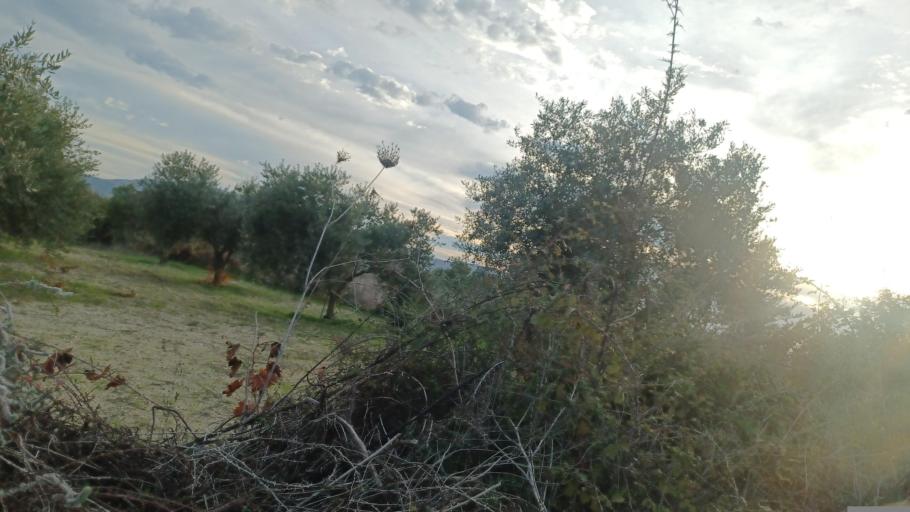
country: CY
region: Pafos
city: Mesogi
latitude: 34.8659
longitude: 32.5141
